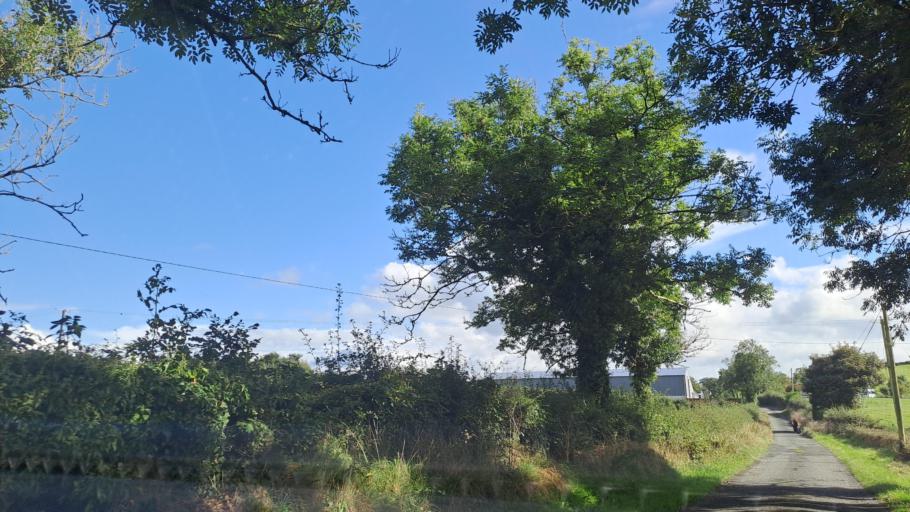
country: IE
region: Ulster
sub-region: An Cabhan
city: Kingscourt
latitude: 53.9943
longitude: -6.8603
